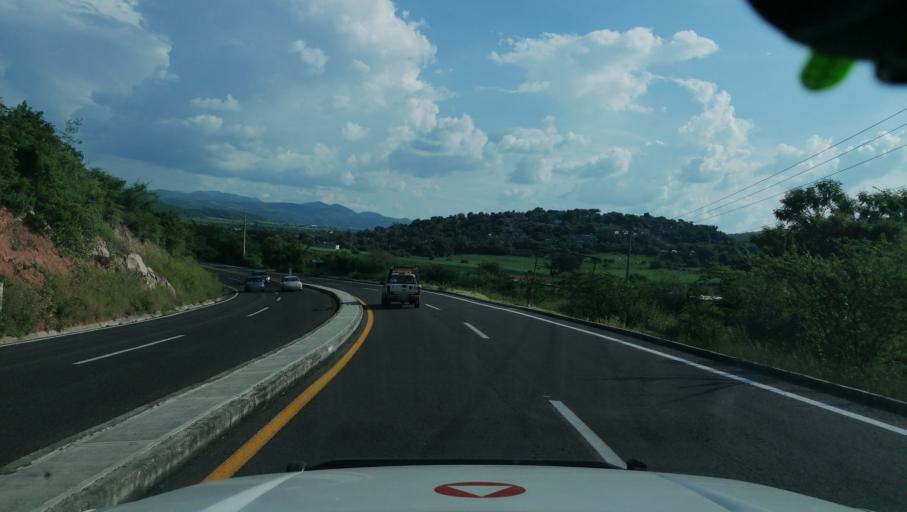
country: MX
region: Morelos
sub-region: Ayala
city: Abelardo L. Rodriguez
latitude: 18.6995
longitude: -98.9940
